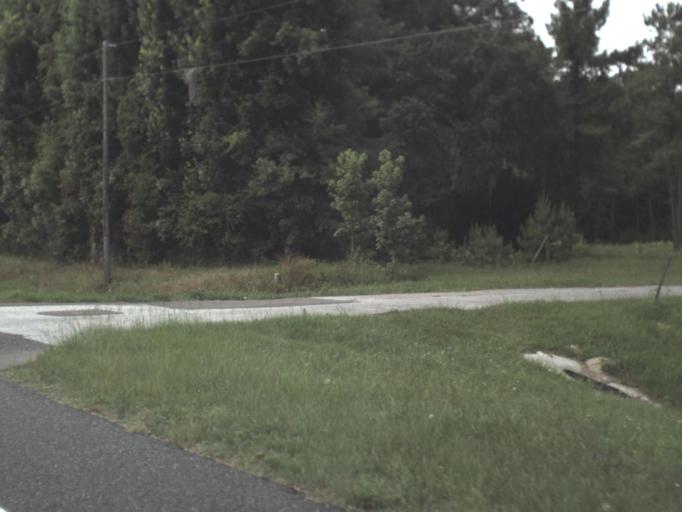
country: US
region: Florida
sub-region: Levy County
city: Chiefland
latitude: 29.4414
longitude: -82.8384
